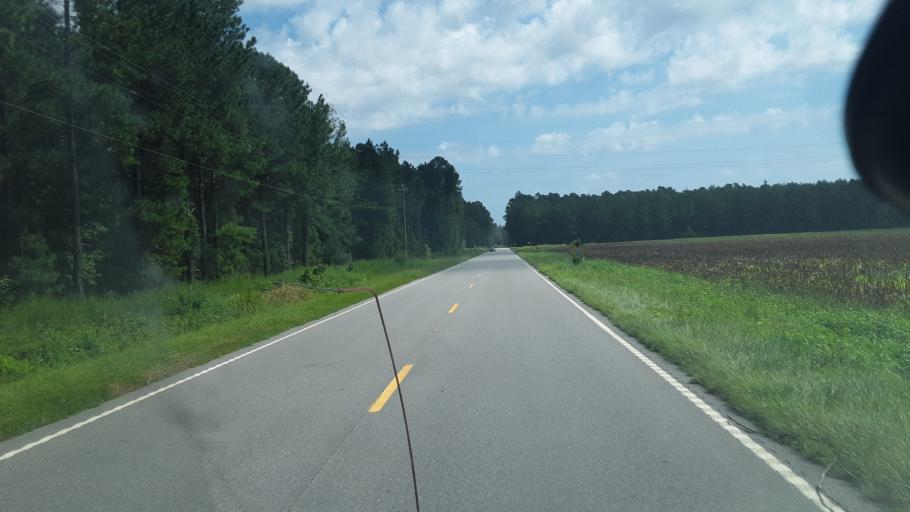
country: US
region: South Carolina
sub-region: Bamberg County
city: Bamberg
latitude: 33.0810
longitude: -81.0207
